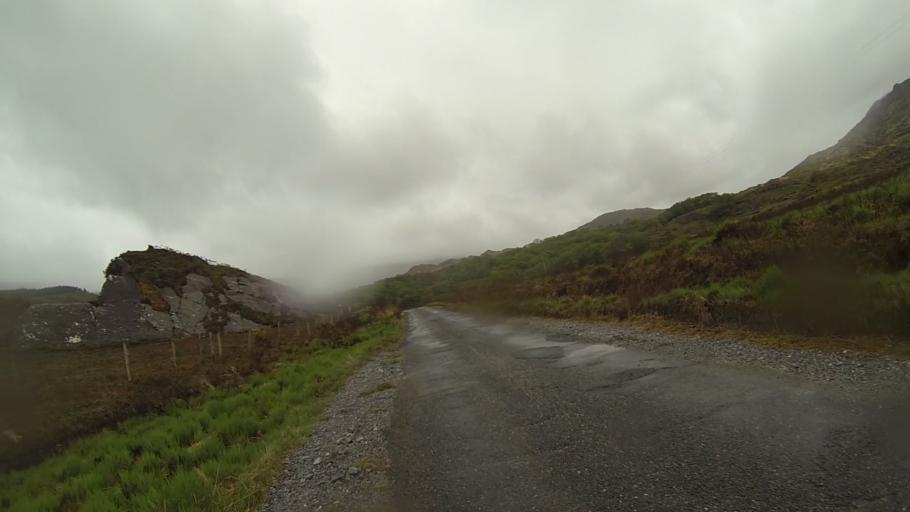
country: IE
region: Munster
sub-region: Ciarrai
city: Kenmare
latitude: 51.9681
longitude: -9.6363
